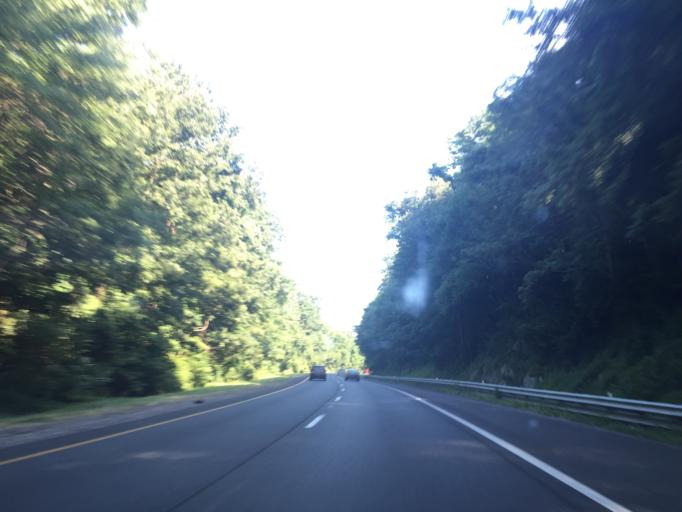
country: US
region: Maryland
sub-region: Baltimore County
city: Hunt Valley
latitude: 39.5764
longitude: -76.6767
